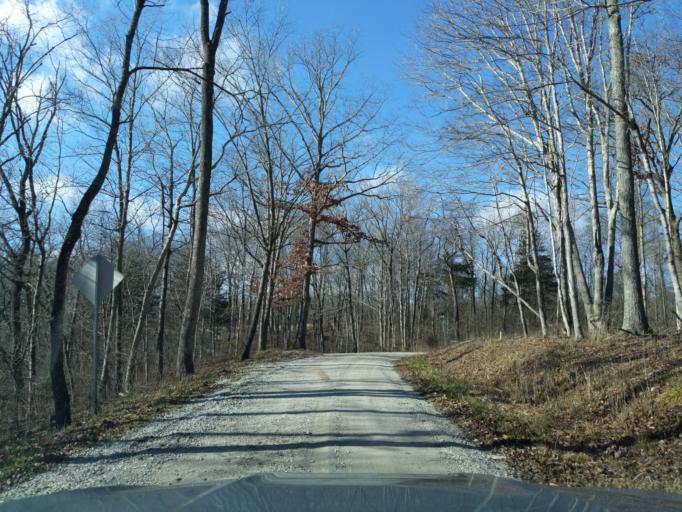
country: US
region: Indiana
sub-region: Decatur County
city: Greensburg
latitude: 39.2401
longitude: -85.4836
